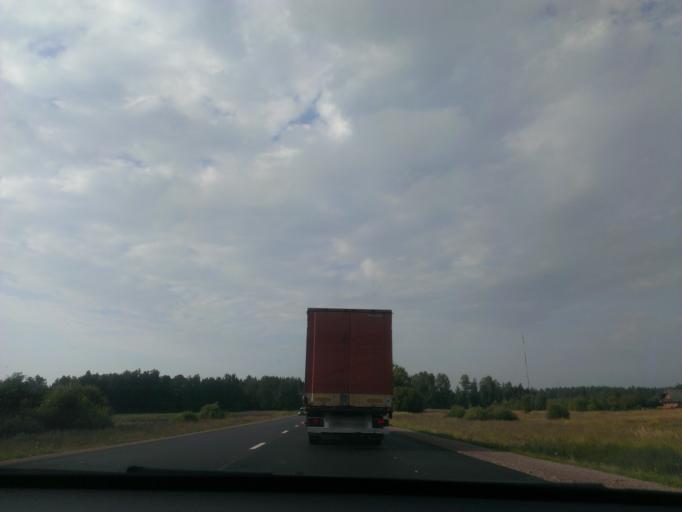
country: LV
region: Lecava
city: Iecava
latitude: 56.6591
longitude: 24.2319
